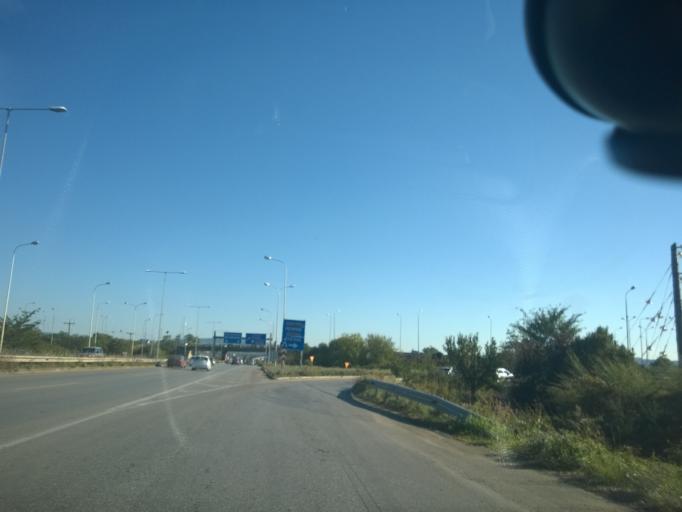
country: GR
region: Central Macedonia
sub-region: Nomos Thessalonikis
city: Thermi
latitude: 40.5410
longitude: 23.0075
